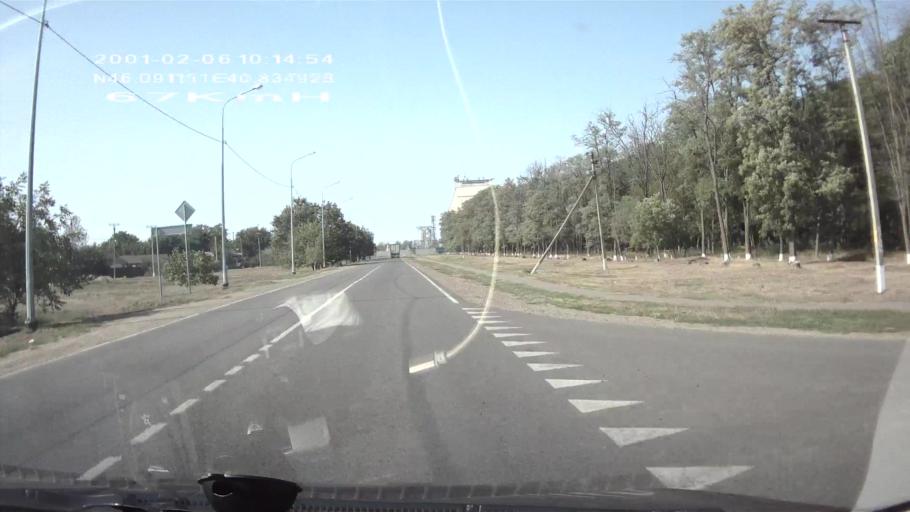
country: RU
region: Krasnodarskiy
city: Belaya Glina
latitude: 46.0911
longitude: 40.8347
